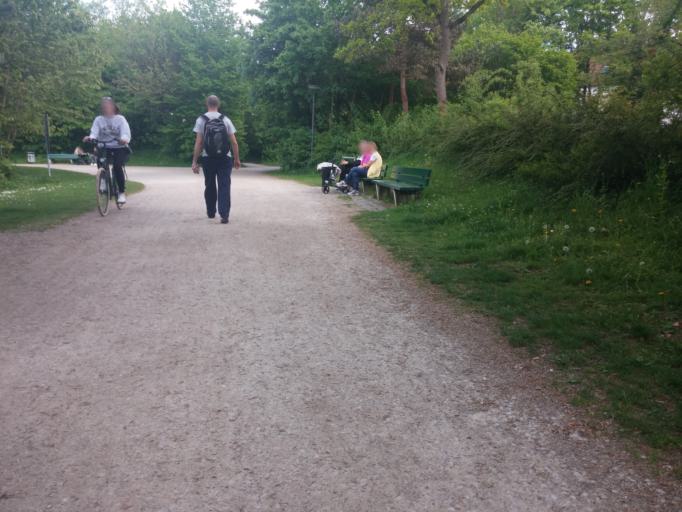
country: DE
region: Bavaria
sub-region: Upper Bavaria
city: Bogenhausen
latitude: 48.1435
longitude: 11.6443
